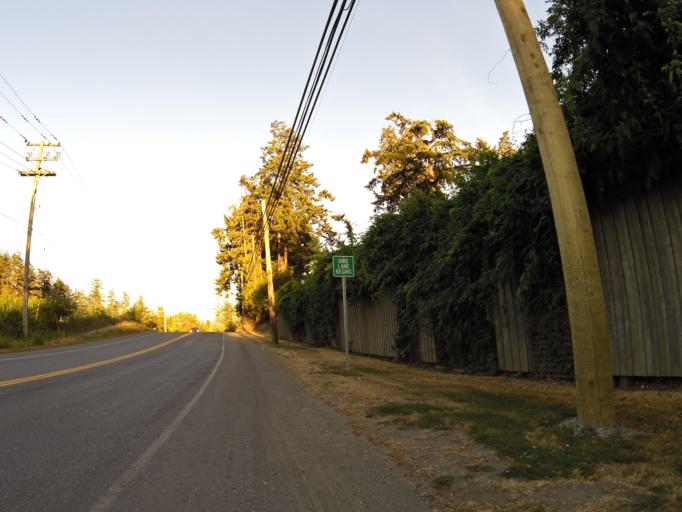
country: CA
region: British Columbia
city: North Cowichan
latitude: 48.8618
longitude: -123.5149
